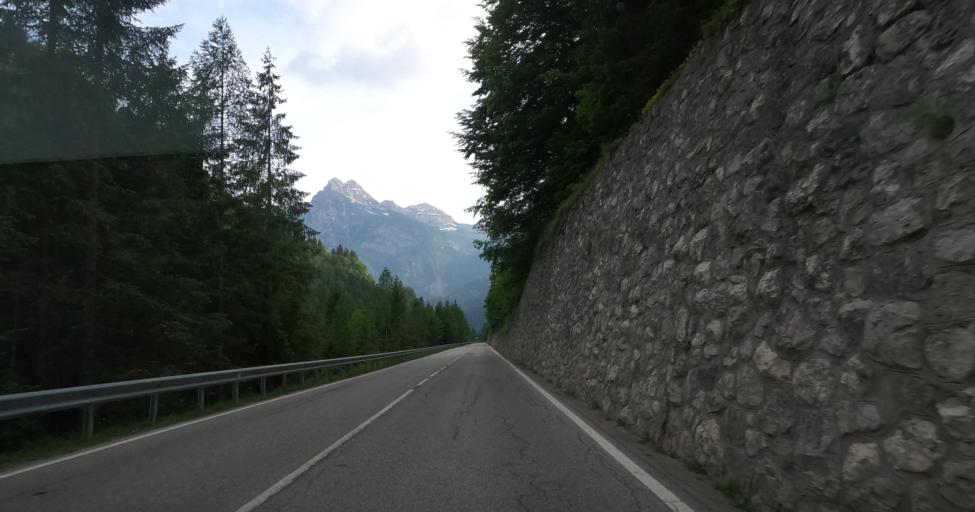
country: IT
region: Veneto
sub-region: Provincia di Belluno
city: Cencenighe Agordino
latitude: 46.3622
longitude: 11.9738
